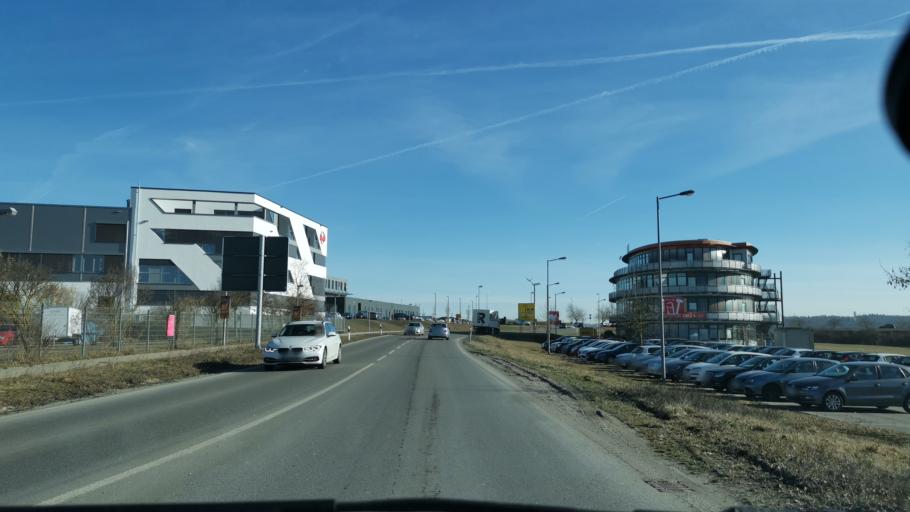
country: DE
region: Baden-Wuerttemberg
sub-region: Regierungsbezirk Stuttgart
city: Gartringen
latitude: 48.6405
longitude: 8.9137
